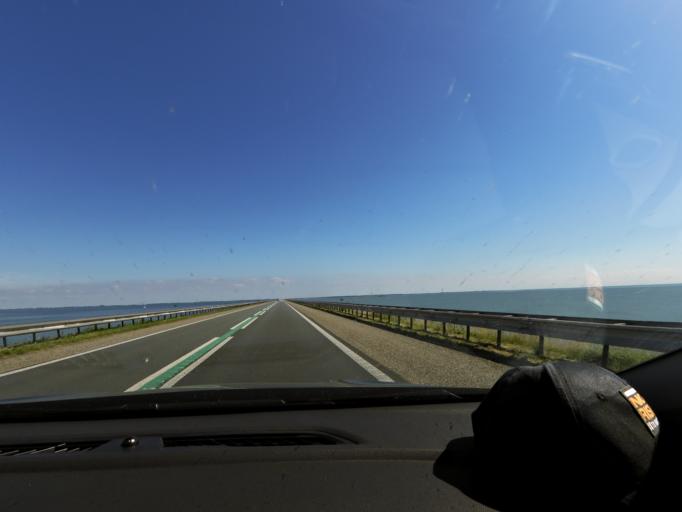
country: NL
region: Flevoland
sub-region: Gemeente Lelystad
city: Lelystad
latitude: 52.6263
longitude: 5.4225
